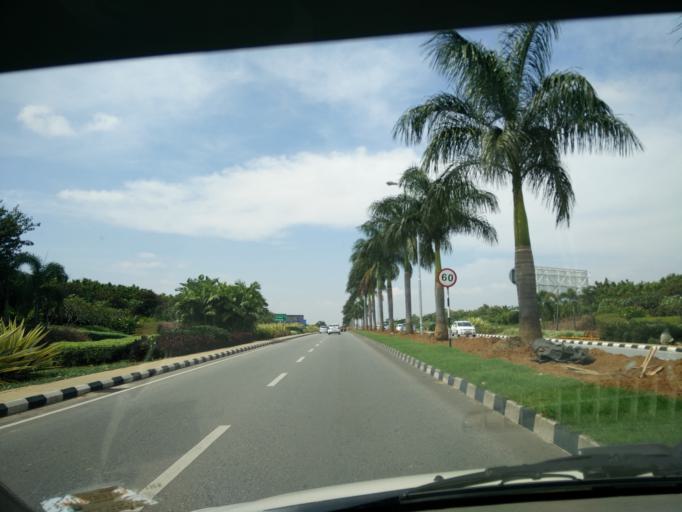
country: IN
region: Karnataka
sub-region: Bangalore Rural
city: Devanhalli
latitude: 13.1980
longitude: 77.6910
